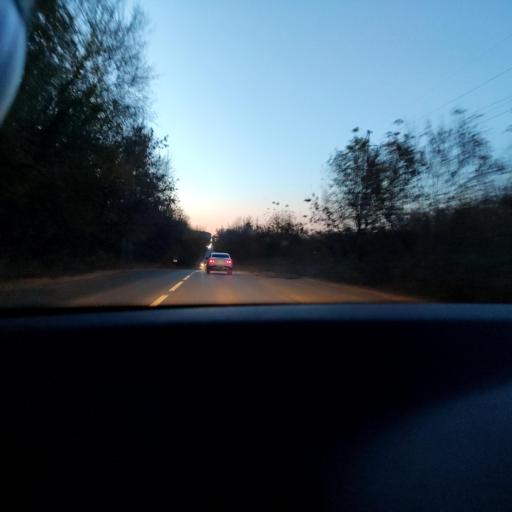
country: RU
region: Samara
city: Petra-Dubrava
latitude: 53.3086
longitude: 50.2773
